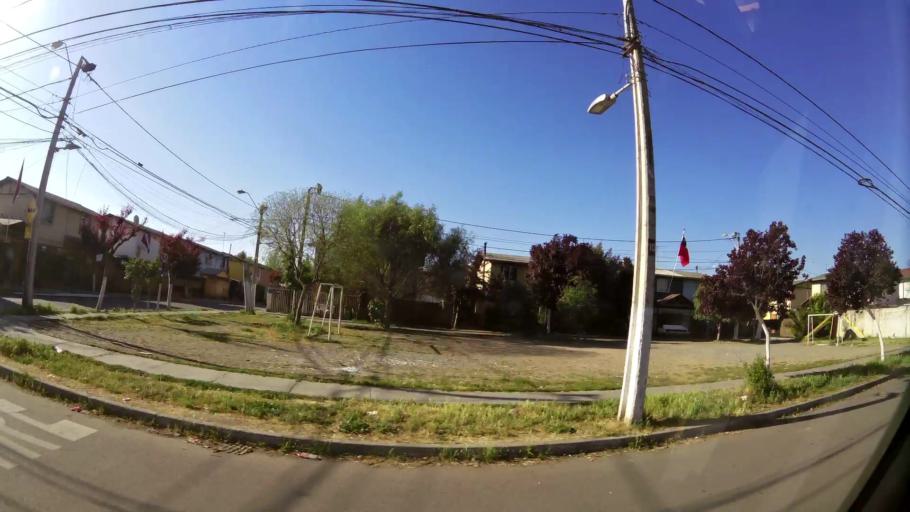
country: CL
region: Santiago Metropolitan
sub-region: Provincia de Talagante
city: Penaflor
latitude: -33.6074
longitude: -70.8654
